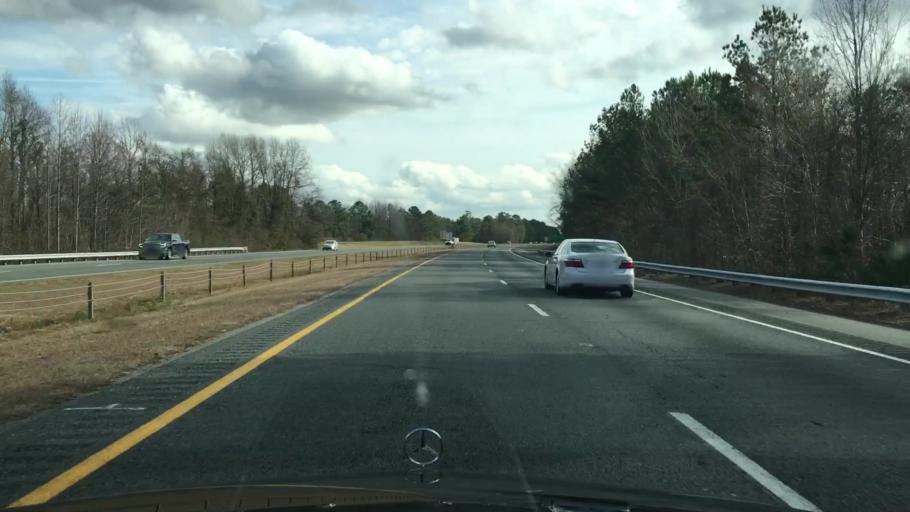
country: US
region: North Carolina
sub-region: Sampson County
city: Plain View
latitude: 35.2215
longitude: -78.3382
